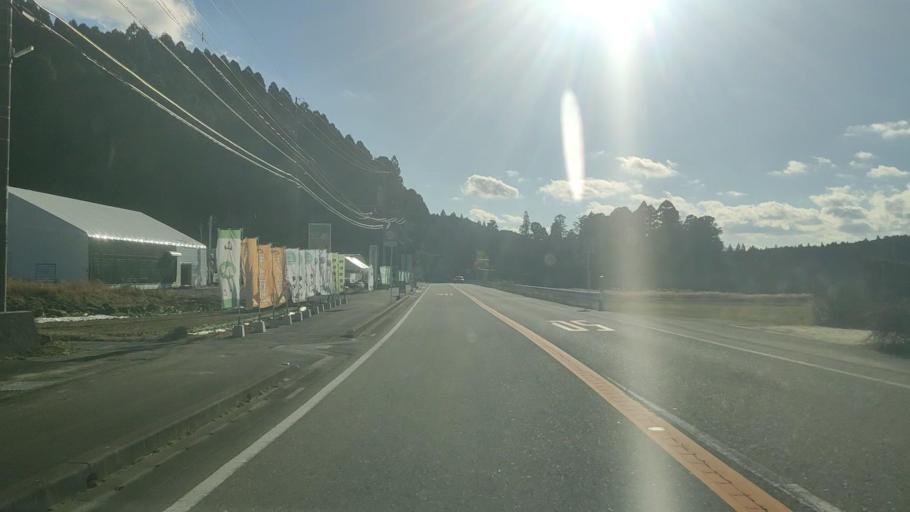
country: JP
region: Fukuoka
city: Maebaru-chuo
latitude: 33.4471
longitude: 130.2721
